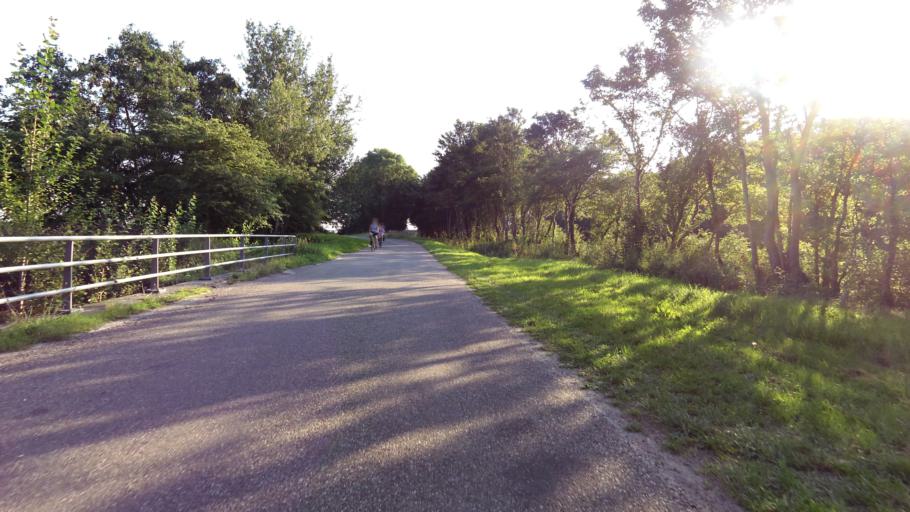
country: NL
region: South Holland
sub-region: Gemeente Noordwijk
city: Noordwijk-Binnen
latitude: 52.2253
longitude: 4.4578
